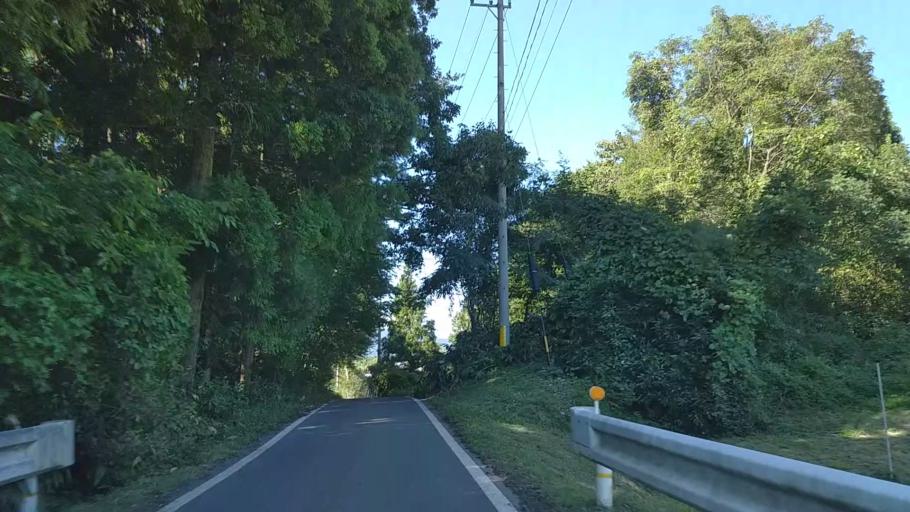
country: JP
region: Nagano
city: Nagano-shi
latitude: 36.5850
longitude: 138.0886
